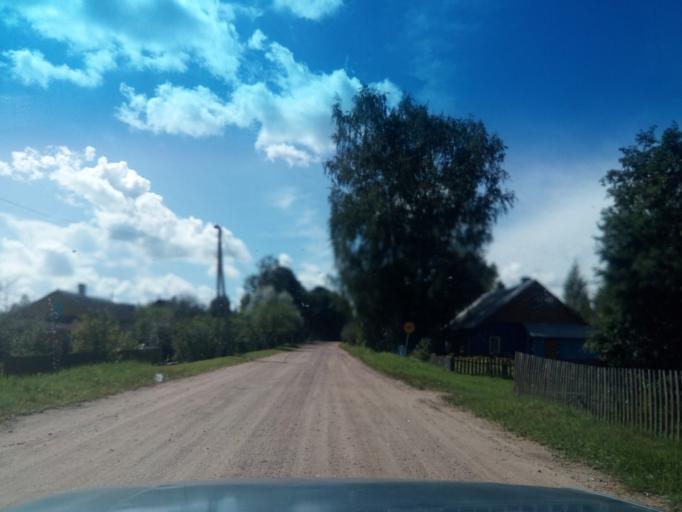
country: BY
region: Vitebsk
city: Dzisna
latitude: 55.6749
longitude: 28.3304
